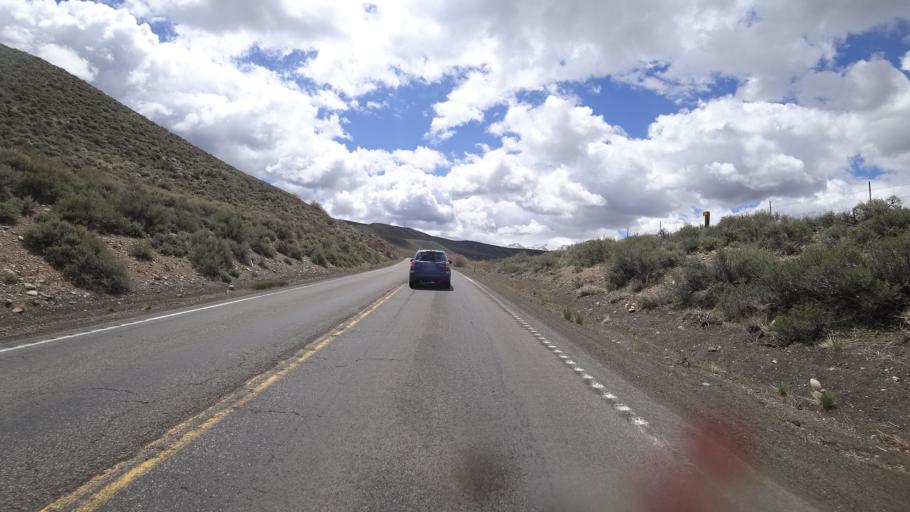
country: US
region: California
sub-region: Mono County
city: Bridgeport
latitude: 38.3634
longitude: -119.4441
